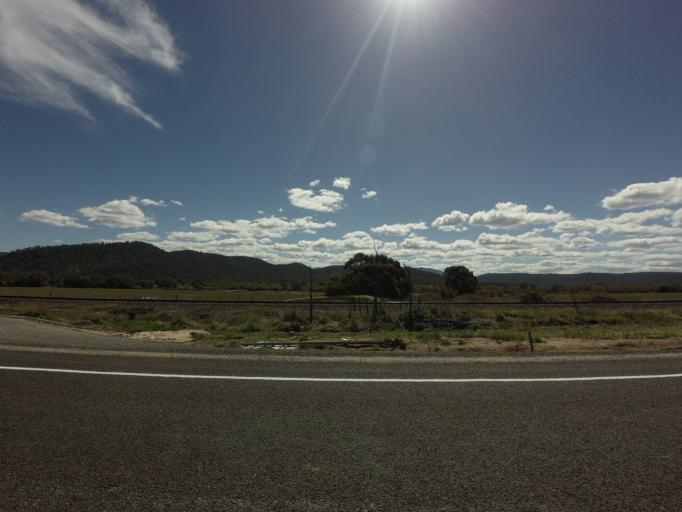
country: AU
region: Tasmania
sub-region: Break O'Day
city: St Helens
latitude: -41.6646
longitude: 147.9105
